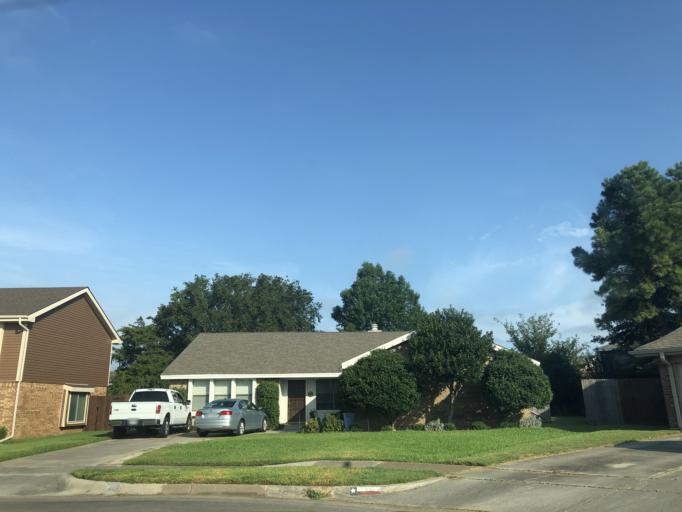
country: US
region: Texas
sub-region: Tarrant County
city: Euless
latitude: 32.8710
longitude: -97.0815
